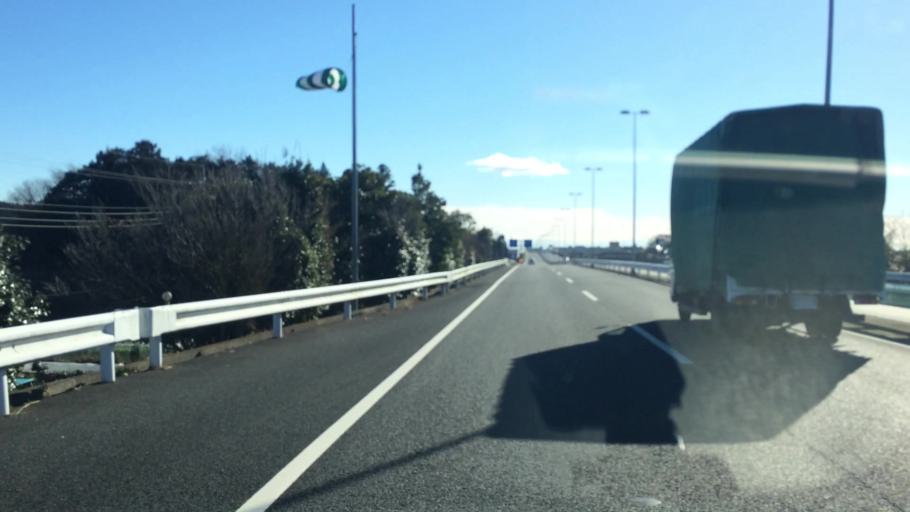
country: JP
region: Tochigi
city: Utsunomiya-shi
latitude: 36.6190
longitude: 139.8585
